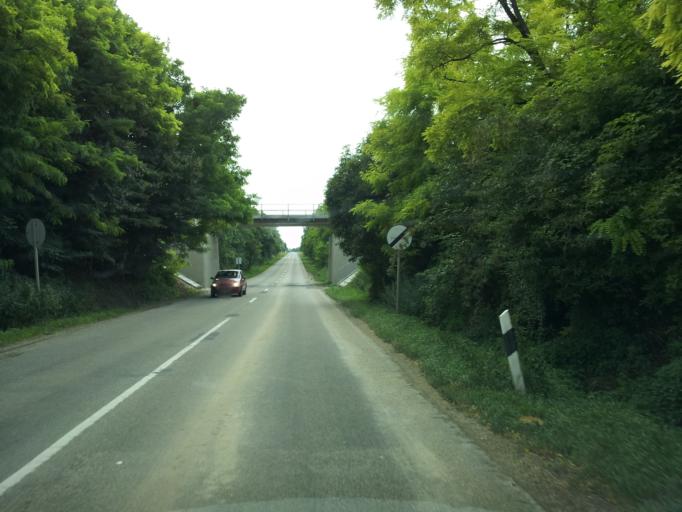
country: HU
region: Fejer
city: Lepseny
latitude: 46.9773
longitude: 18.2120
